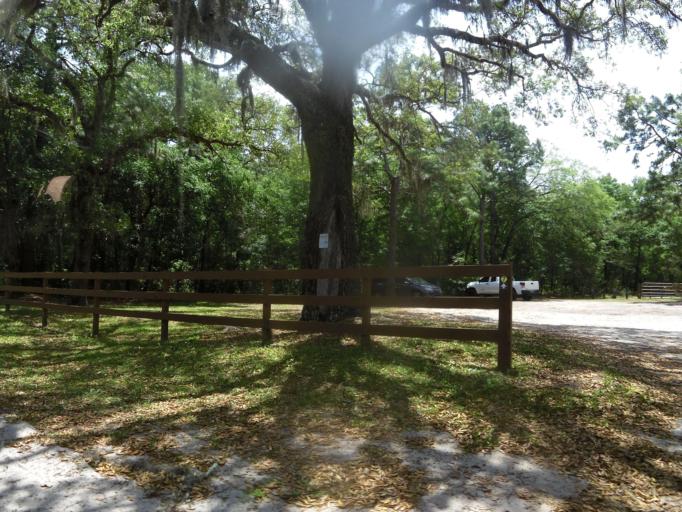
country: US
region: Florida
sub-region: Duval County
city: Atlantic Beach
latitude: 30.4622
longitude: -81.4885
